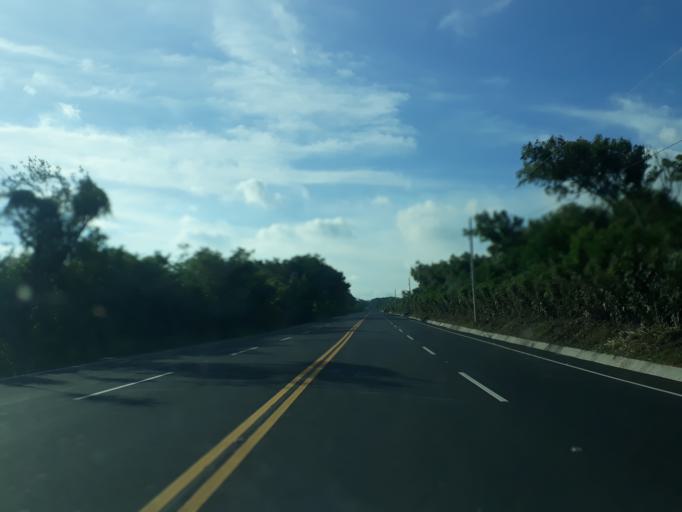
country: NI
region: Carazo
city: Diriamba
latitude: 11.9082
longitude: -86.2638
